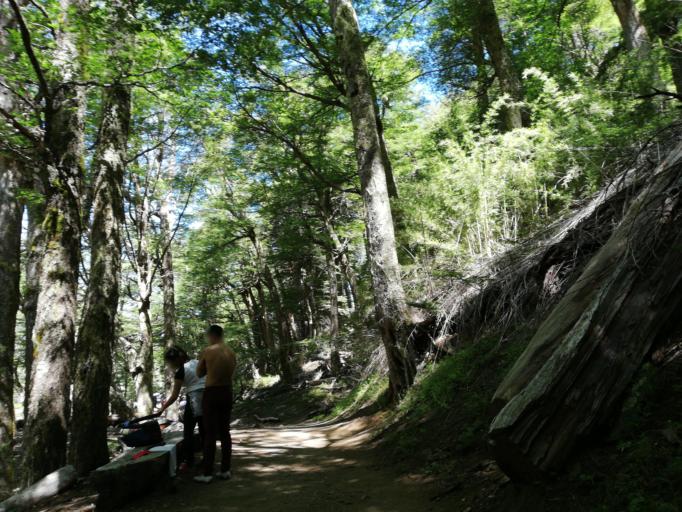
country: AR
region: Neuquen
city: Villa La Angostura
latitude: -41.1930
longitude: -71.8332
